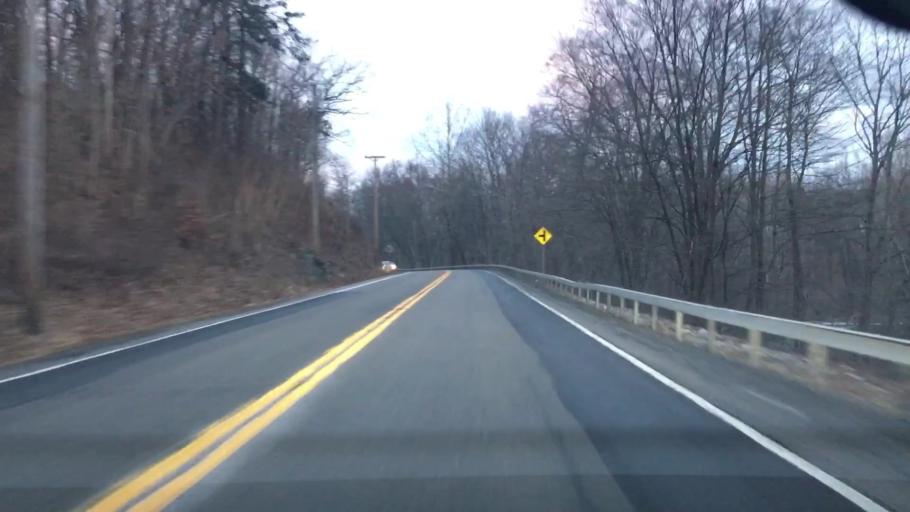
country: US
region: New York
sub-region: Dutchess County
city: Red Oaks Mill
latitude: 41.6657
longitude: -73.8774
